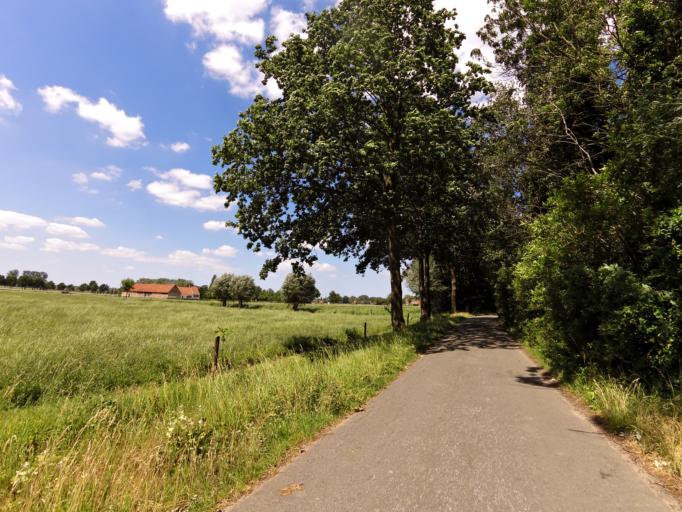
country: BE
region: Flanders
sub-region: Provincie West-Vlaanderen
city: Zedelgem
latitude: 51.1589
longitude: 3.1182
